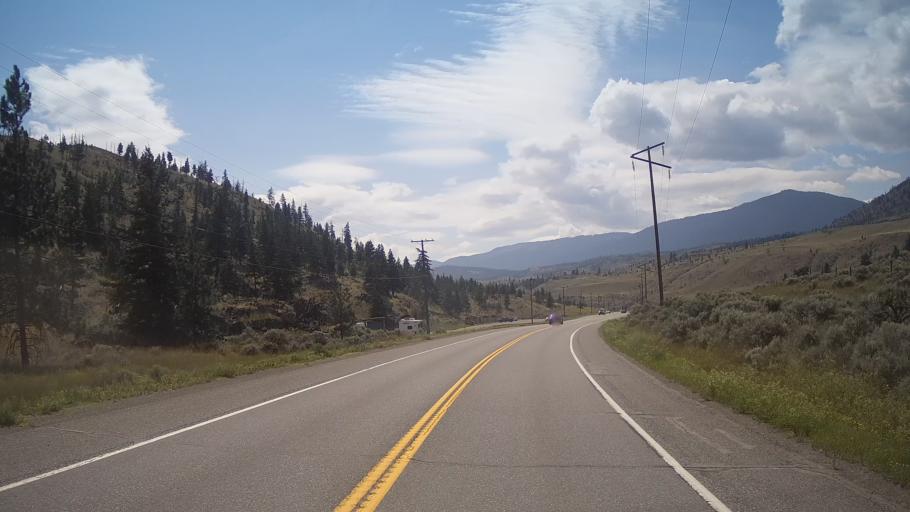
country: CA
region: British Columbia
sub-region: Thompson-Nicola Regional District
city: Ashcroft
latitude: 50.6404
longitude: -121.3436
